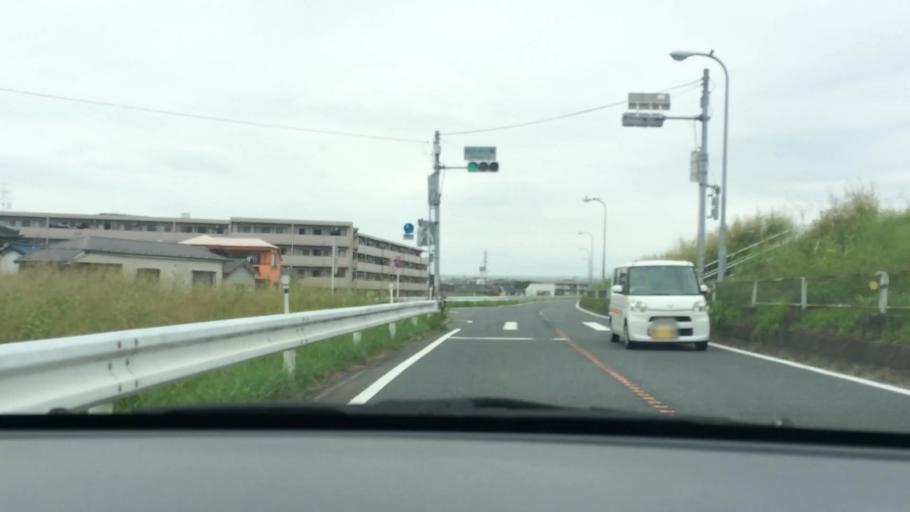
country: JP
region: Chiba
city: Matsudo
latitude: 35.7726
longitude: 139.8798
